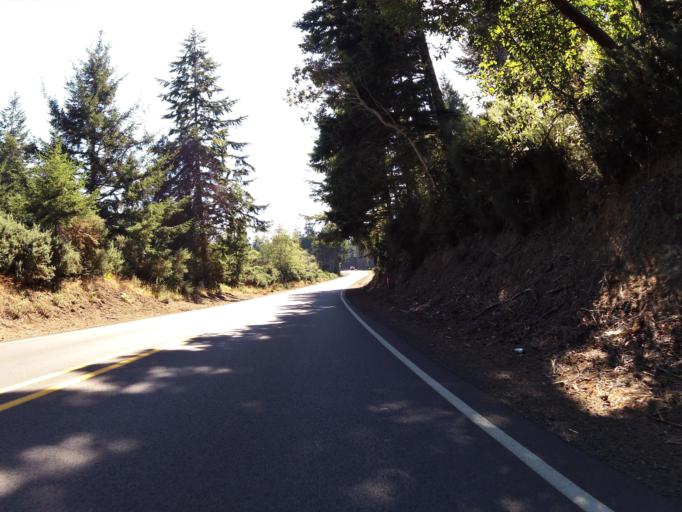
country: US
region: Oregon
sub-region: Coos County
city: Bandon
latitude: 43.1951
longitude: -124.3662
